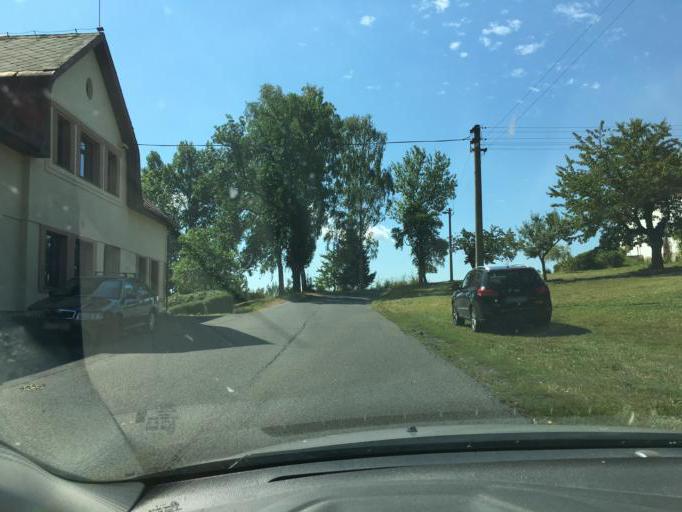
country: CZ
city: Plavy
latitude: 50.7027
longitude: 15.3480
